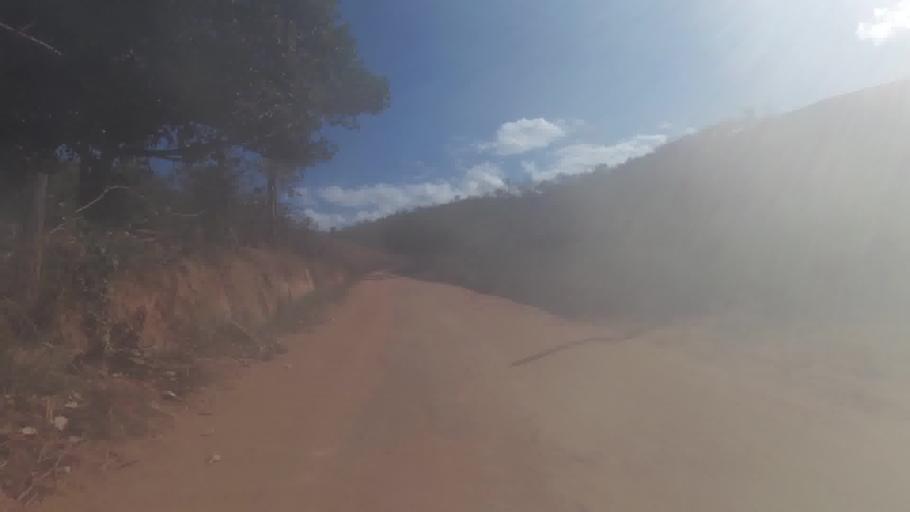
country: BR
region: Espirito Santo
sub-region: Cachoeiro De Itapemirim
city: Cachoeiro de Itapemirim
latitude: -21.0300
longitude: -41.0562
